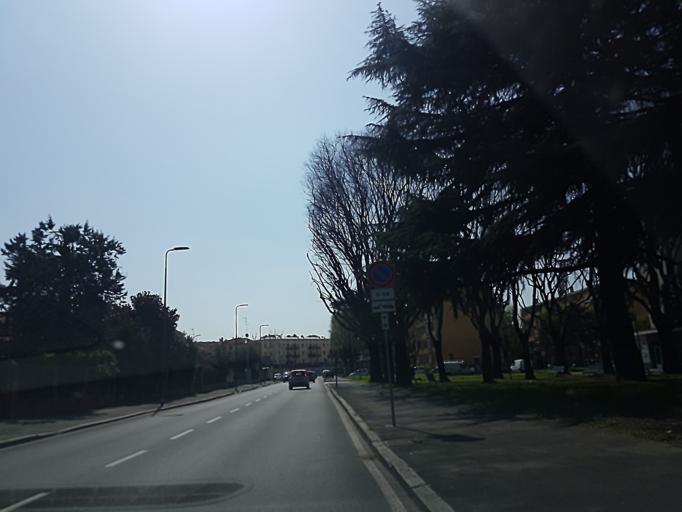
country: IT
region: Lombardy
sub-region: Citta metropolitana di Milano
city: Romano Banco
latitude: 45.4498
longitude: 9.1306
